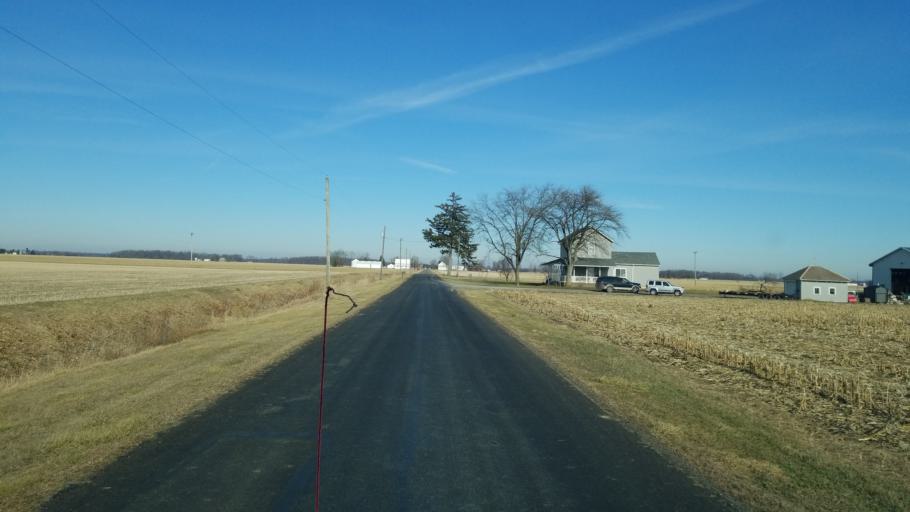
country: US
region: Ohio
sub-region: Putnam County
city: Pandora
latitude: 40.9757
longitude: -83.9382
